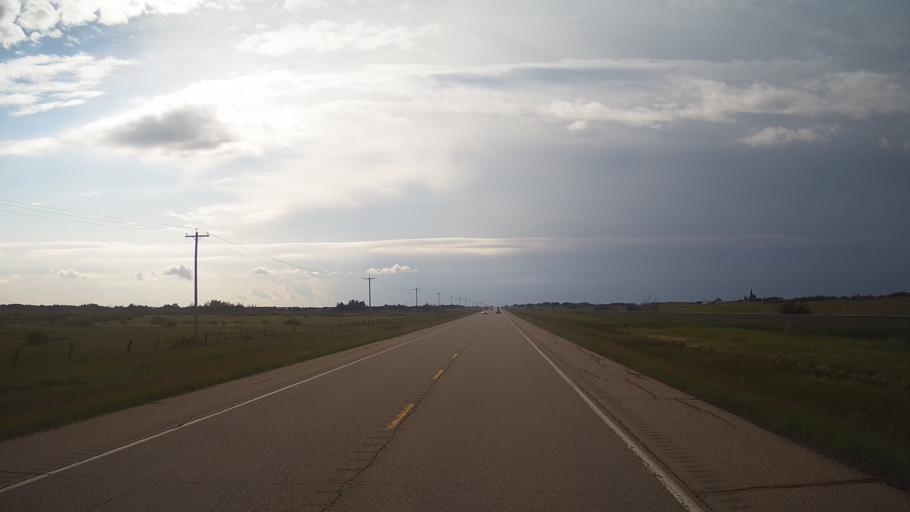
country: CA
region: Alberta
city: Viking
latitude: 53.1424
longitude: -111.9438
